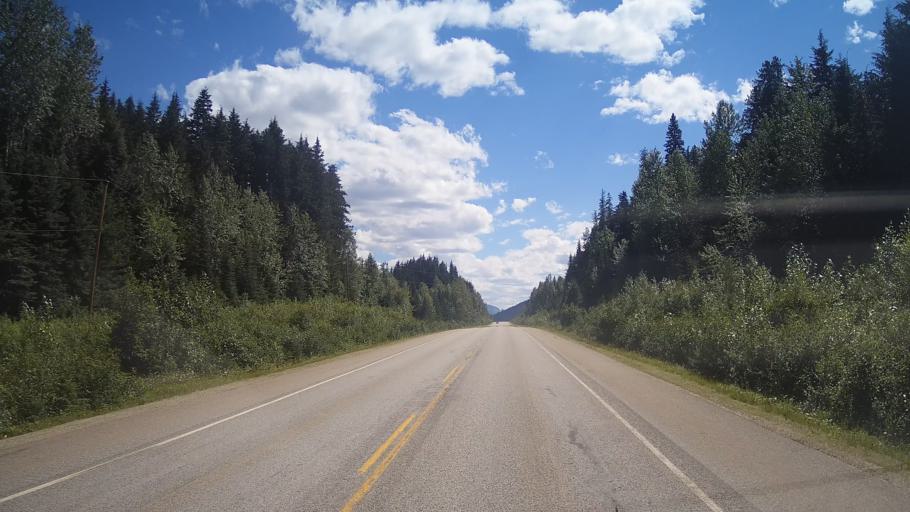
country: CA
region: Alberta
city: Jasper Park Lodge
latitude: 52.5550
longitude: -119.1114
